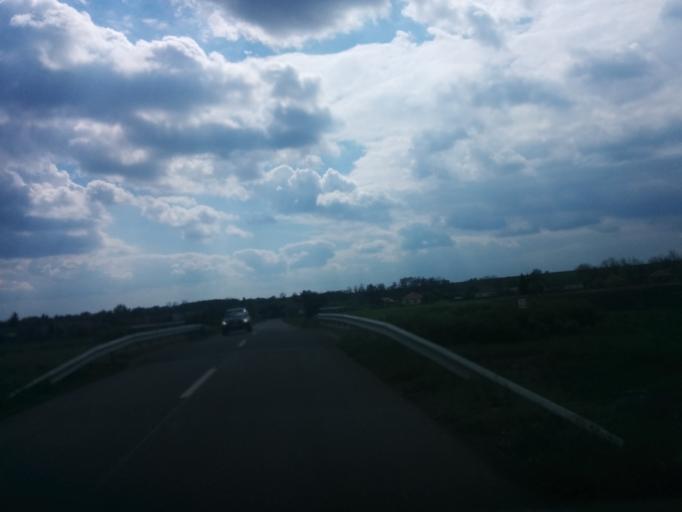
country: HU
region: Nograd
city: Jobbagyi
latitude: 47.8275
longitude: 19.6452
